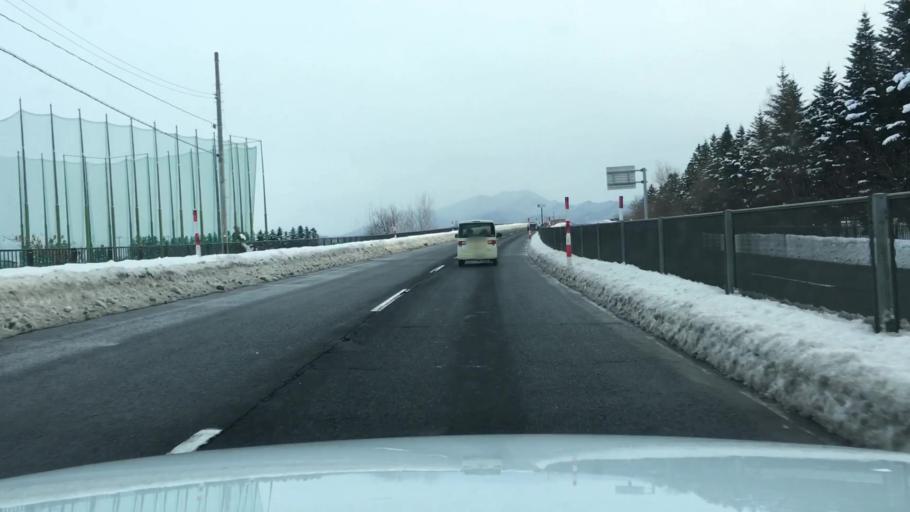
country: JP
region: Aomori
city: Hirosaki
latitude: 40.5918
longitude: 140.5060
